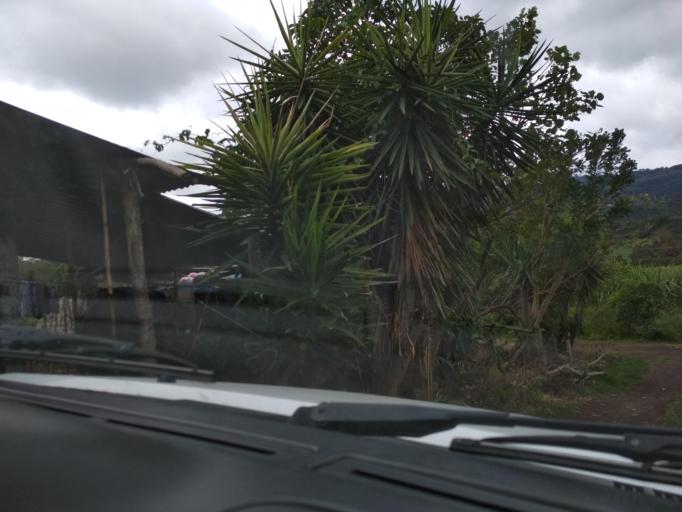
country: MX
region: Veracruz
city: El Castillo
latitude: 19.5832
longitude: -96.8404
